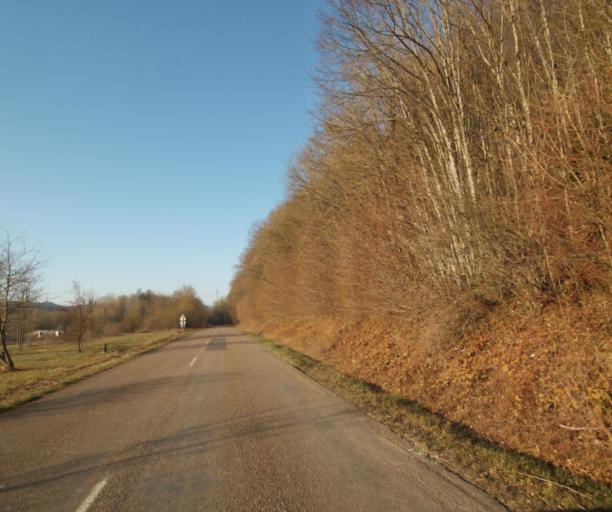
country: FR
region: Champagne-Ardenne
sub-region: Departement de la Haute-Marne
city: Chevillon
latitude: 48.5272
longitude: 5.1107
